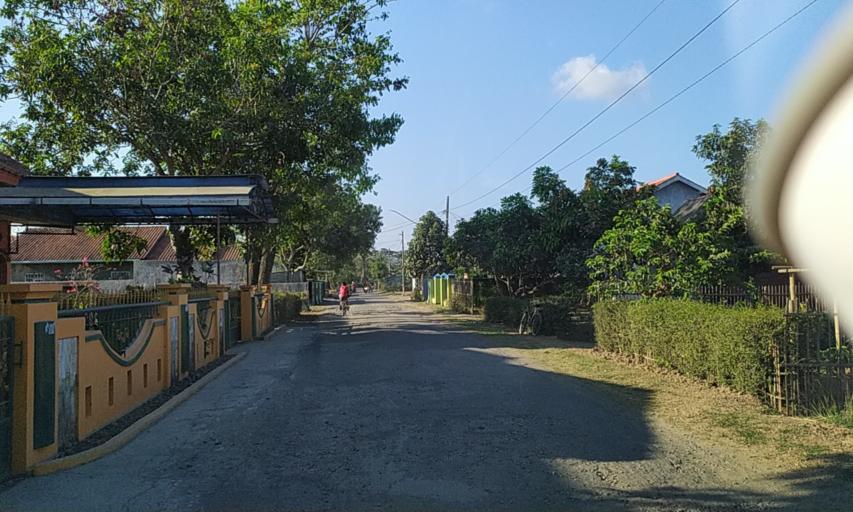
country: ID
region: Central Java
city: Karangrena
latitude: -7.6054
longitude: 109.1292
